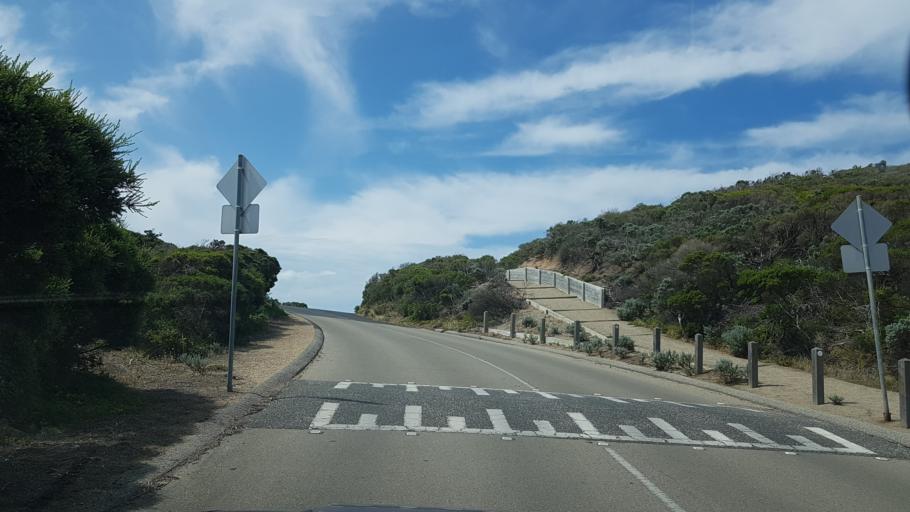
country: AU
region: Victoria
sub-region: Mornington Peninsula
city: Sorrento
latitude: -38.3347
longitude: 144.7064
